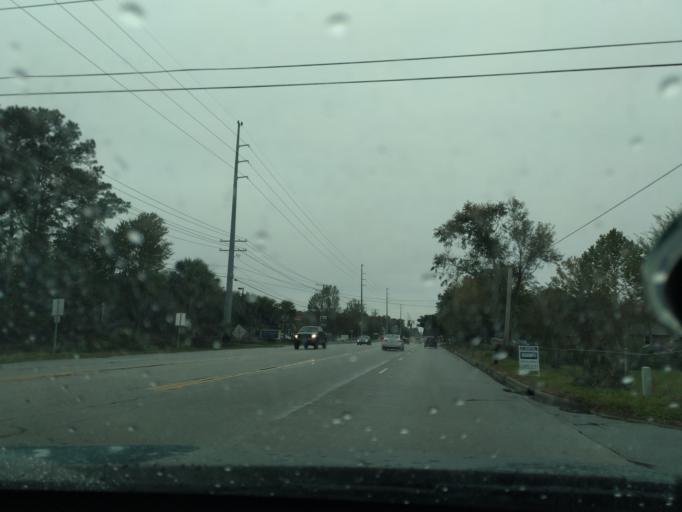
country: US
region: South Carolina
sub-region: Charleston County
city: Folly Beach
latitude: 32.7149
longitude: -79.9652
